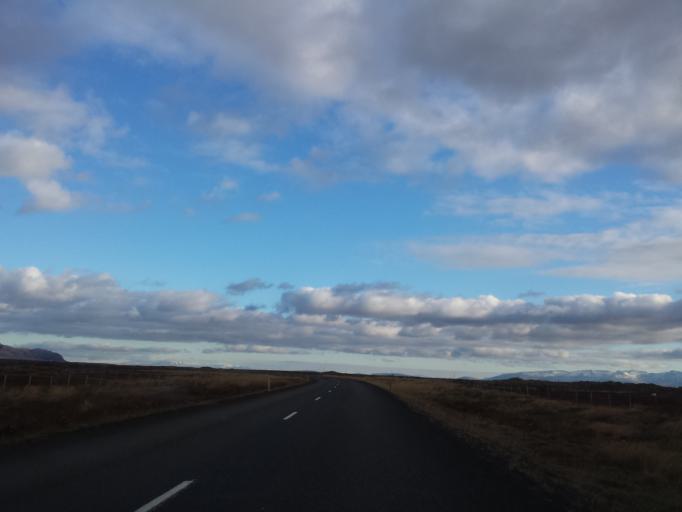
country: IS
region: West
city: Borgarnes
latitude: 64.6980
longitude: -22.1289
